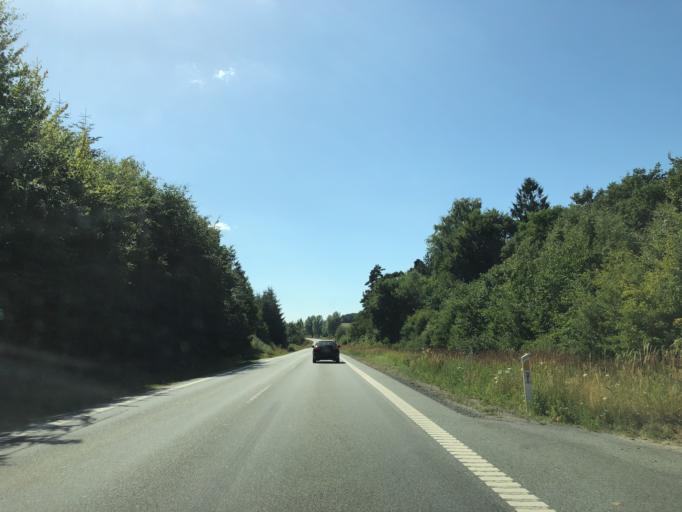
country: DK
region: North Denmark
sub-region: Mariagerfjord Kommune
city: Hobro
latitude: 56.6149
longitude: 9.6984
